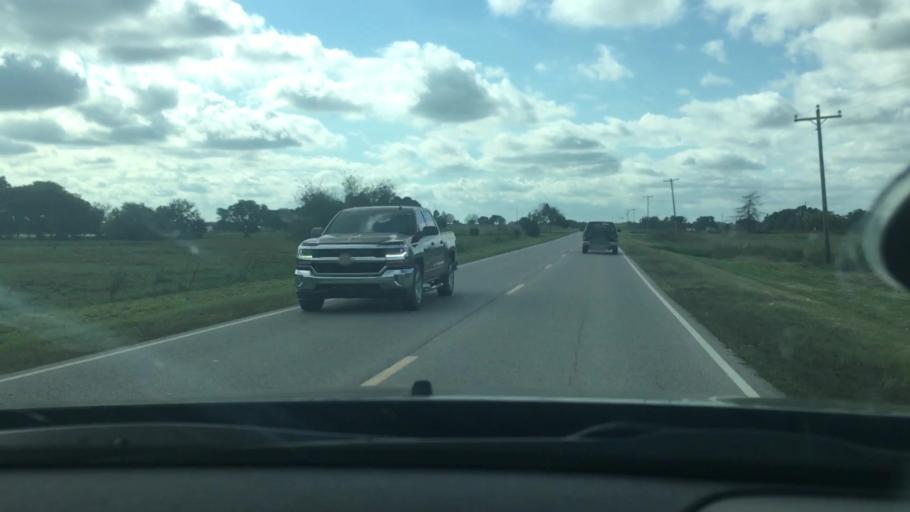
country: US
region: Oklahoma
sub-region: Pontotoc County
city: Ada
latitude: 34.7185
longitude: -96.6349
